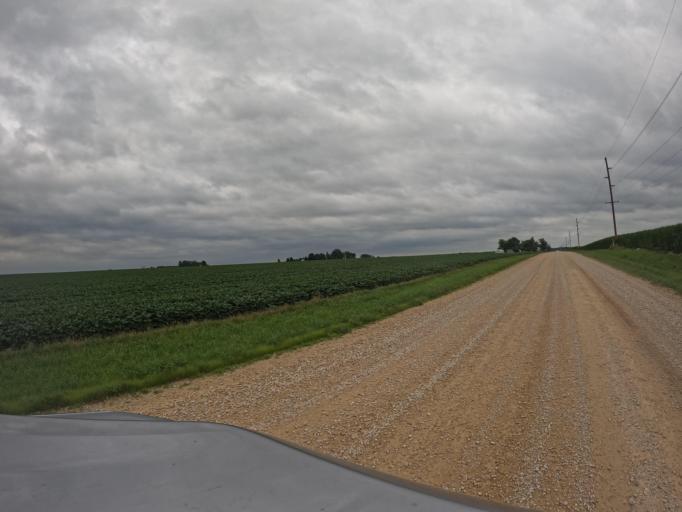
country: US
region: Iowa
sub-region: Clinton County
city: De Witt
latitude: 41.8042
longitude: -90.4714
